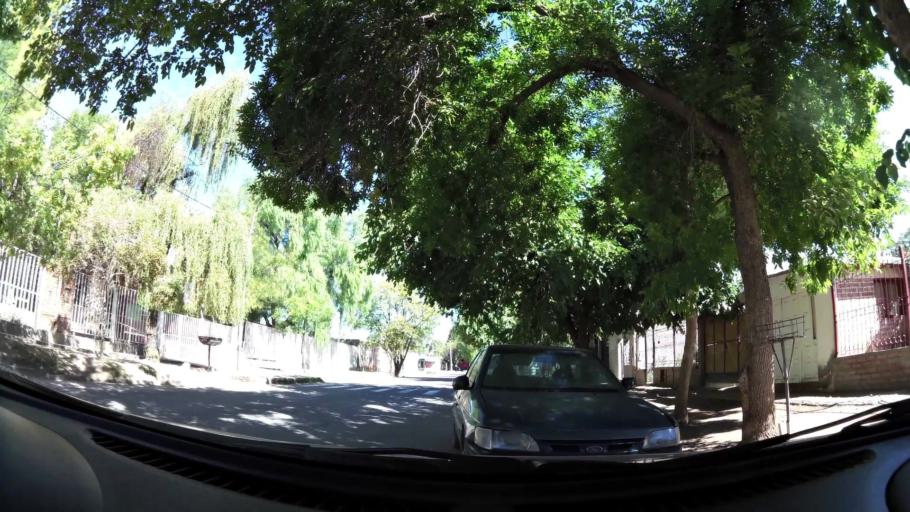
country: AR
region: Mendoza
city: Las Heras
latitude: -32.8301
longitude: -68.8224
